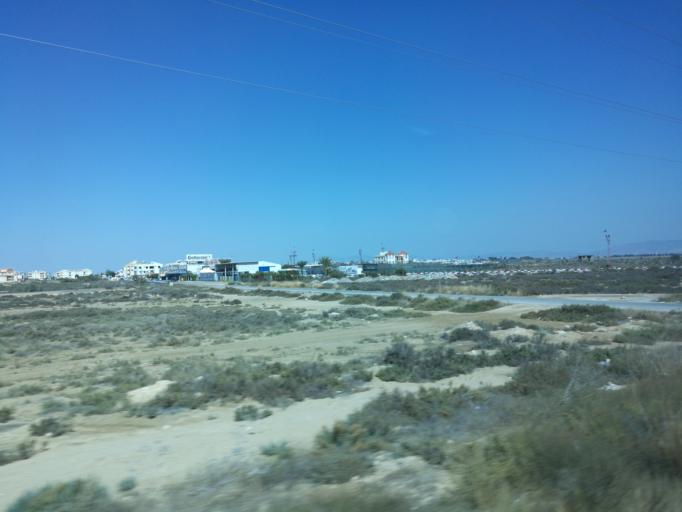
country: CY
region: Ammochostos
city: Famagusta
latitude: 35.1597
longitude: 33.8998
